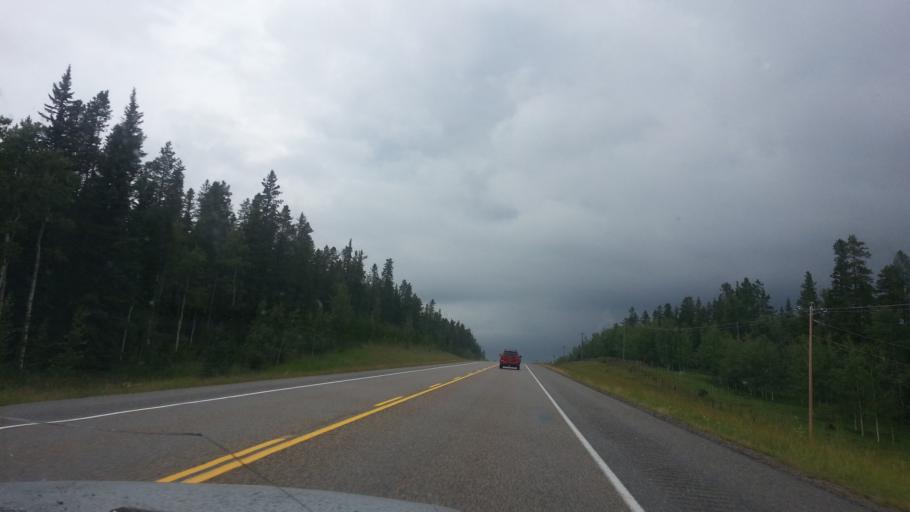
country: CA
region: Alberta
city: Cochrane
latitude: 50.9293
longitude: -114.5602
